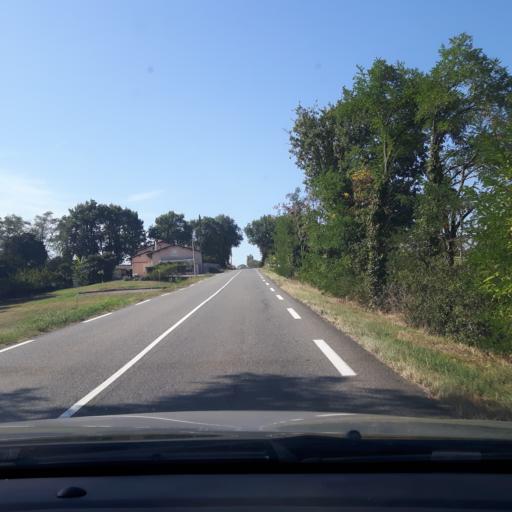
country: FR
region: Midi-Pyrenees
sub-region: Departement de la Haute-Garonne
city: Montjoire
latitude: 43.7653
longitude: 1.5285
